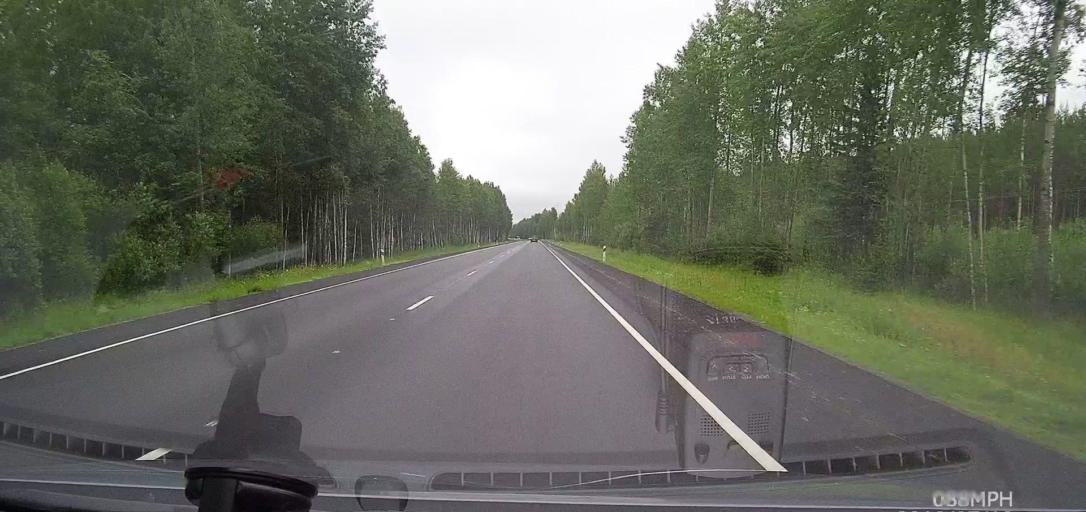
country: RU
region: Leningrad
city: Syas'stroy
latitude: 60.2358
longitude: 32.7421
